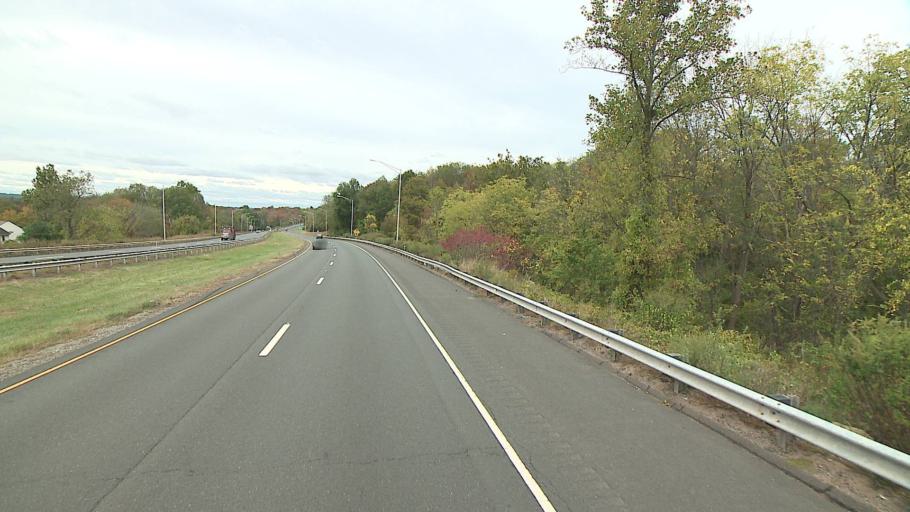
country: US
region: Connecticut
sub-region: Middlesex County
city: Middletown
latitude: 41.5359
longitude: -72.6194
